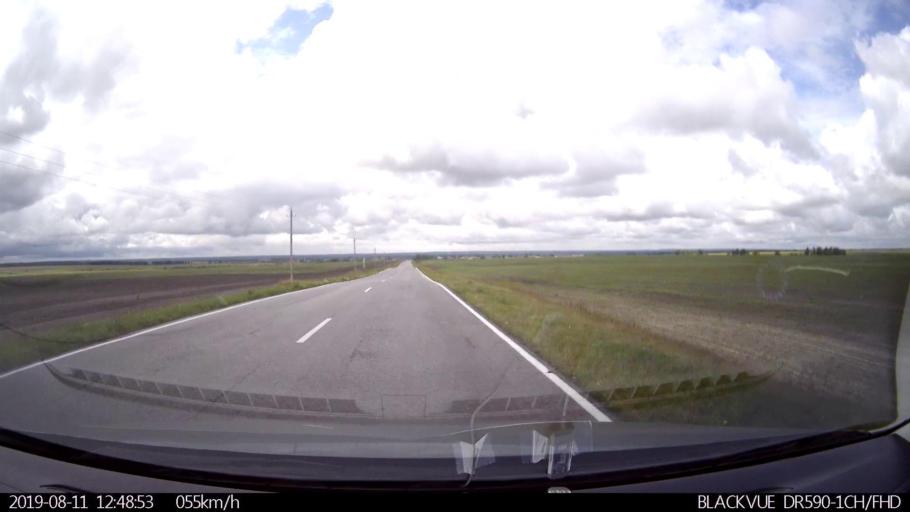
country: RU
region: Ulyanovsk
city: Ignatovka
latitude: 53.8744
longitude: 47.6942
